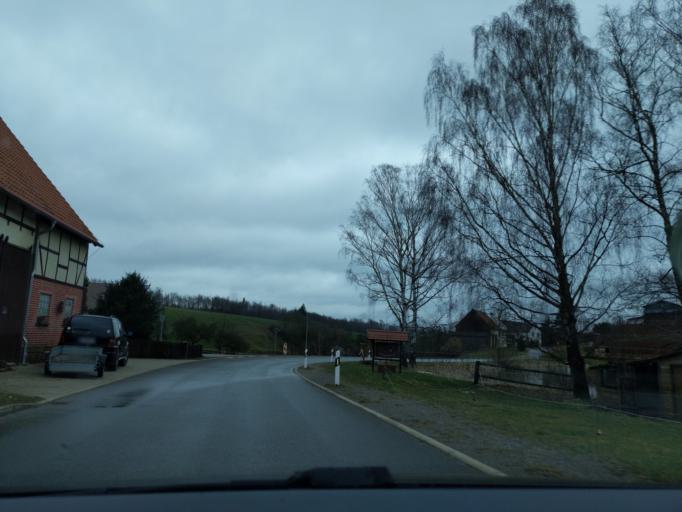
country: DE
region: Hesse
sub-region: Regierungsbezirk Kassel
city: Bad Arolsen
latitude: 51.3250
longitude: 9.0495
